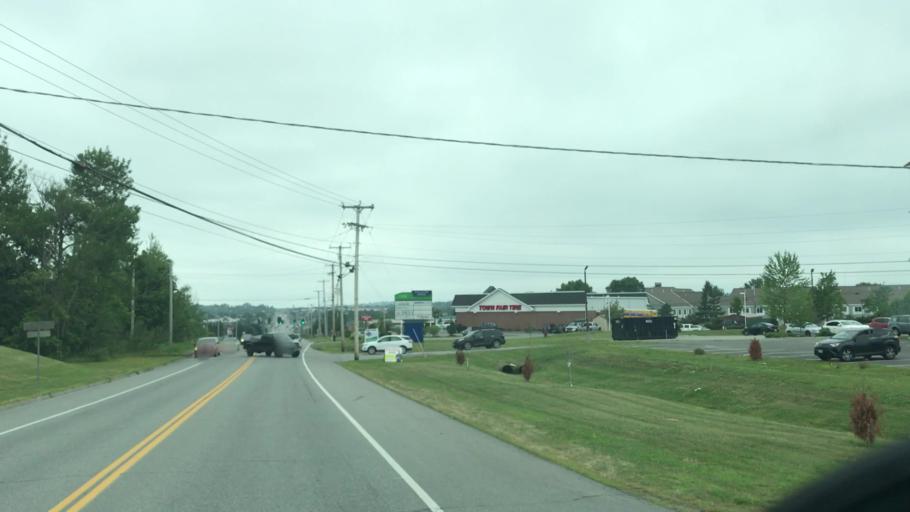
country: US
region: Maine
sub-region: Penobscot County
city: Veazie
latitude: 44.8424
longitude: -68.7431
